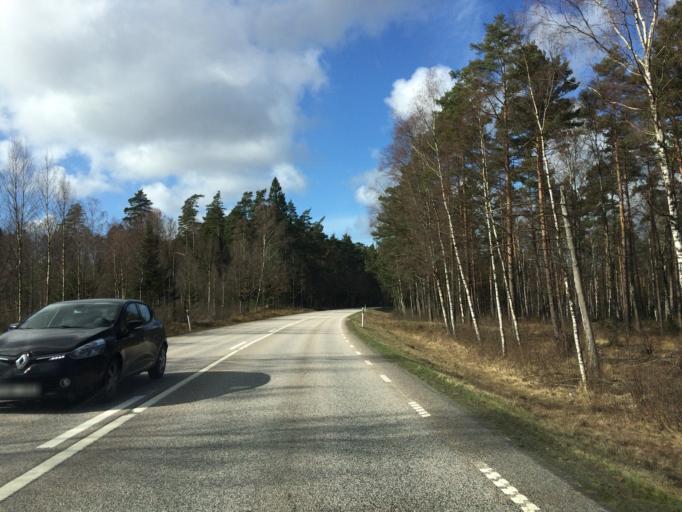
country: SE
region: Halland
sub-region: Laholms Kommun
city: Knared
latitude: 56.4943
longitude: 13.3858
